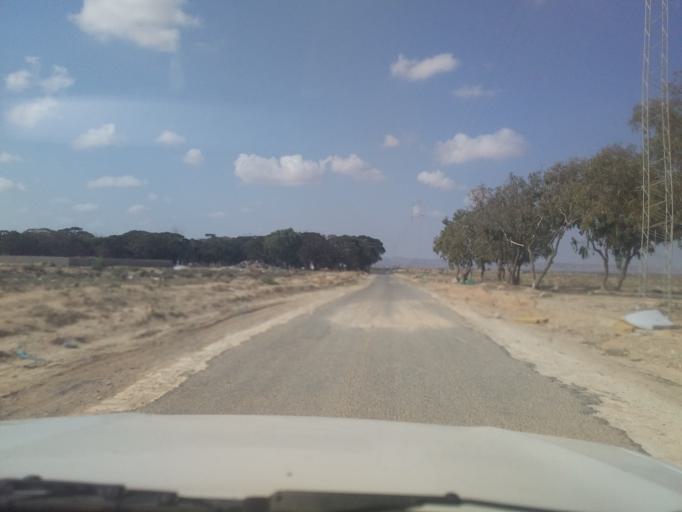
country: TN
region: Qabis
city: Gabes
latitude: 33.6301
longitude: 10.2725
